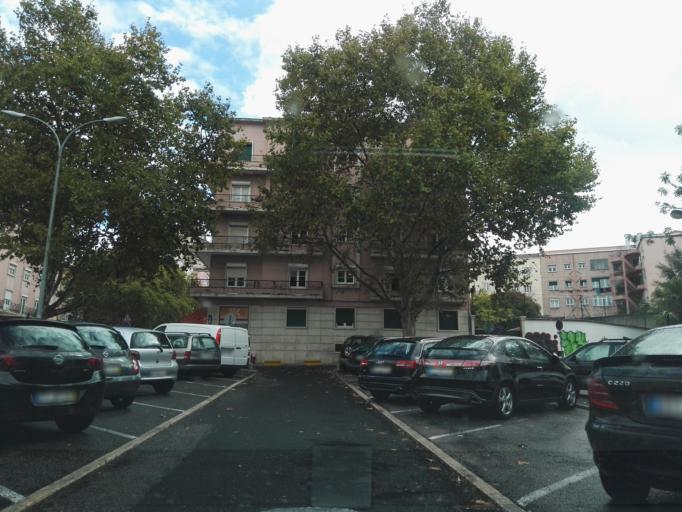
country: PT
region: Lisbon
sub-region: Lisbon
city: Lisbon
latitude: 38.7445
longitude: -9.1349
